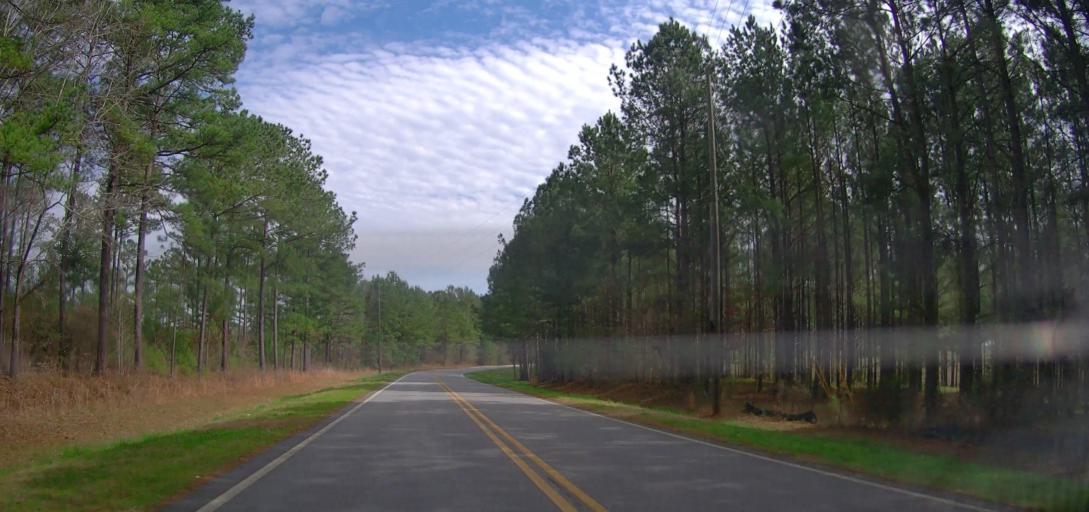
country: US
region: Georgia
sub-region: Jones County
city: Gray
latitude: 33.0642
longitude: -83.7276
